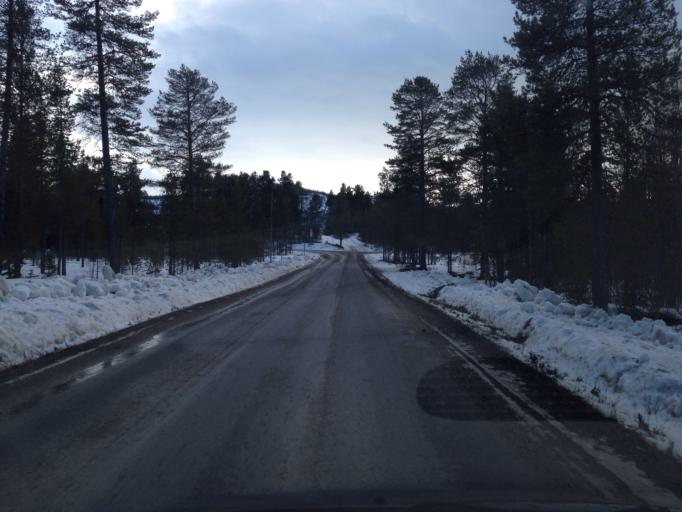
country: SE
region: Jaemtland
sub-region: Harjedalens Kommun
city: Sveg
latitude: 62.1143
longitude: 13.2633
